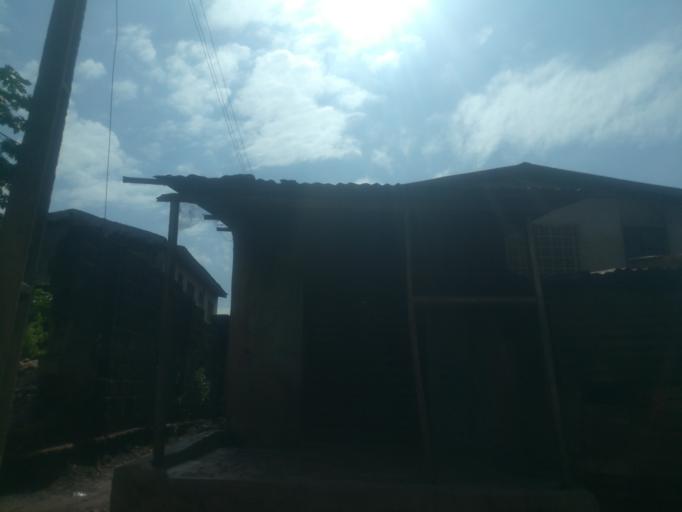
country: NG
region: Oyo
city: Ibadan
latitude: 7.4210
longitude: 3.9757
